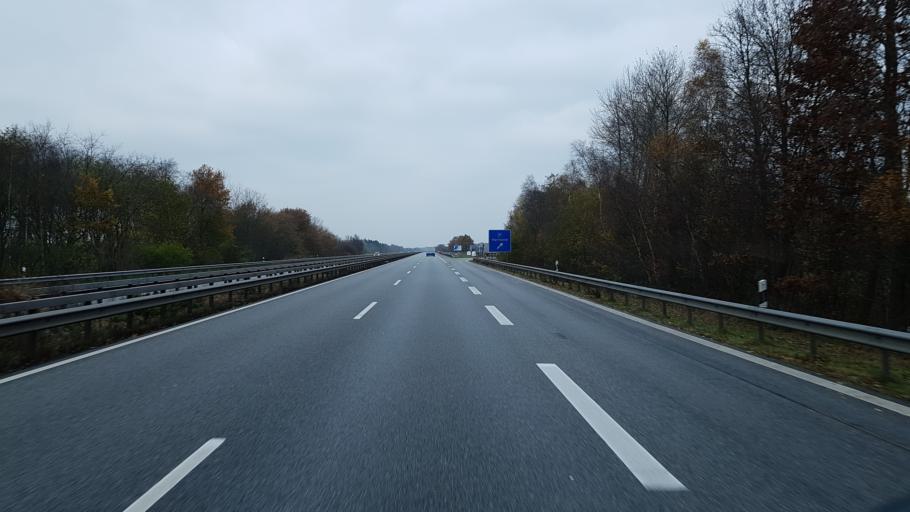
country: DE
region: Lower Saxony
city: Uthlede
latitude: 53.3397
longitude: 8.6090
